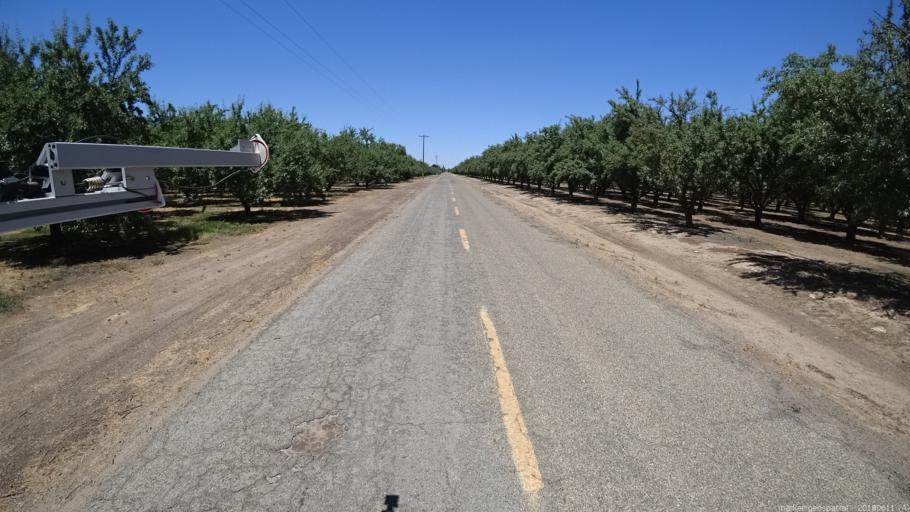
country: US
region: California
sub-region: Madera County
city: Fairmead
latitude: 37.0637
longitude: -120.2115
